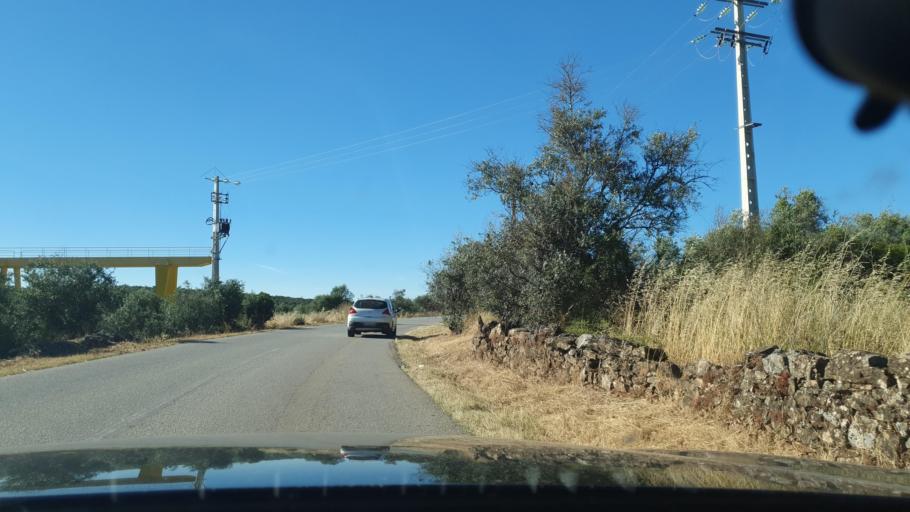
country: PT
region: Evora
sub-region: Vila Vicosa
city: Vila Vicosa
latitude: 38.7479
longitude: -7.4090
